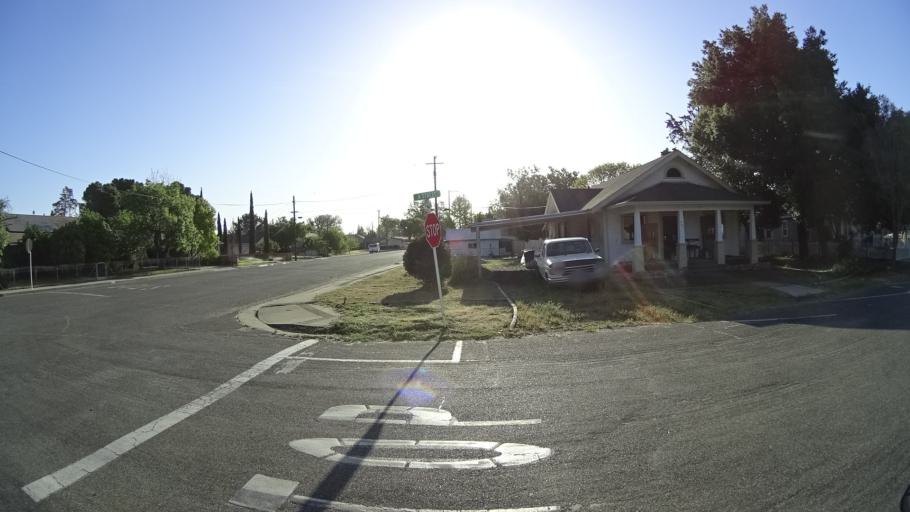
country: US
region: California
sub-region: Glenn County
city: Orland
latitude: 39.7509
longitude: -122.1890
